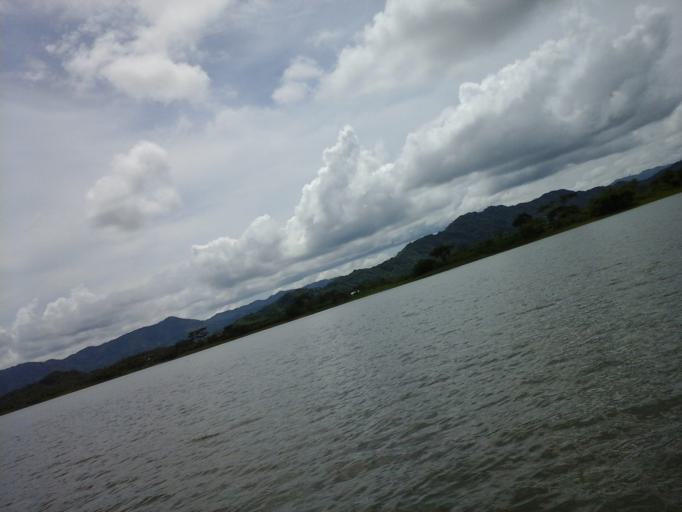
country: CO
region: Bolivar
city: San Cristobal
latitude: 9.8731
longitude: -75.2984
